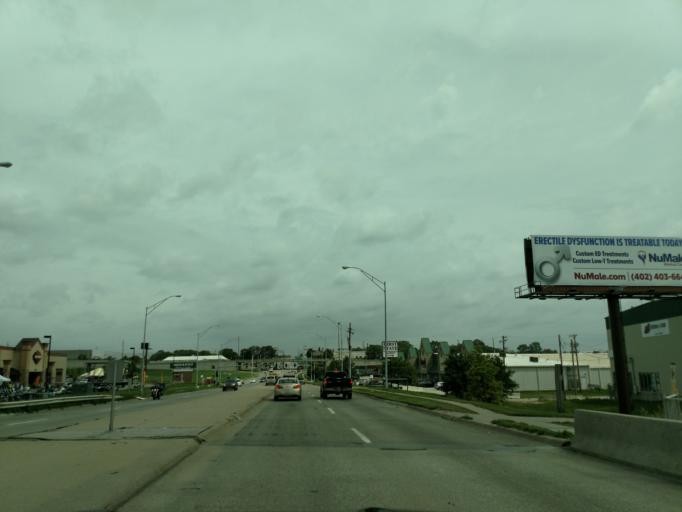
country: US
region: Nebraska
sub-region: Douglas County
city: Ralston
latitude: 41.2089
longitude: -96.0238
